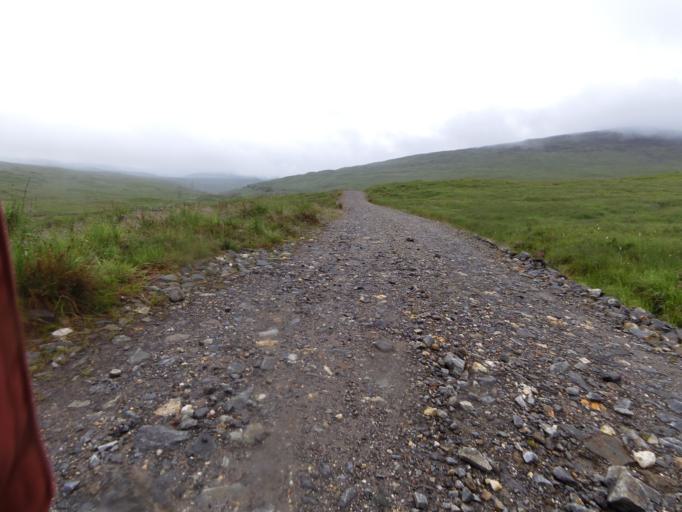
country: GB
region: Scotland
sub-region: Highland
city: Spean Bridge
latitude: 56.7729
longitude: -4.7063
